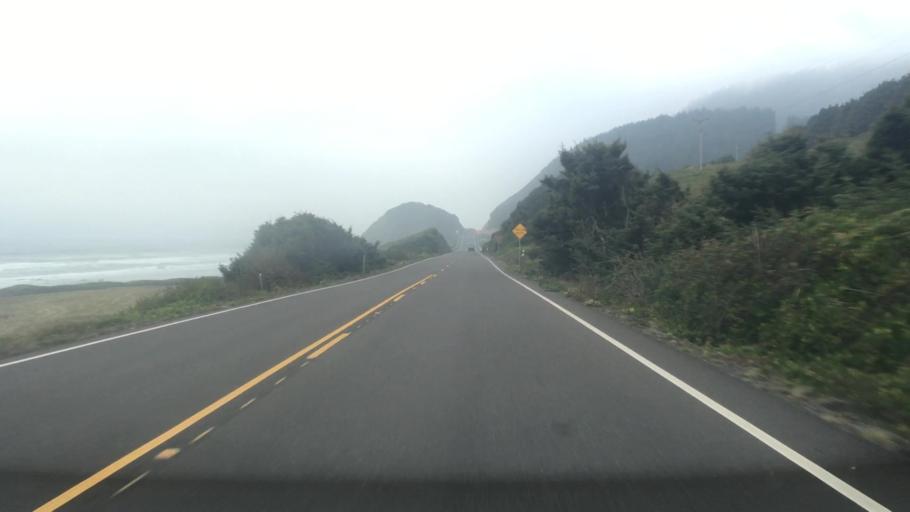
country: US
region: Oregon
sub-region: Lane County
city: Florence
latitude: 44.1801
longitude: -124.1151
